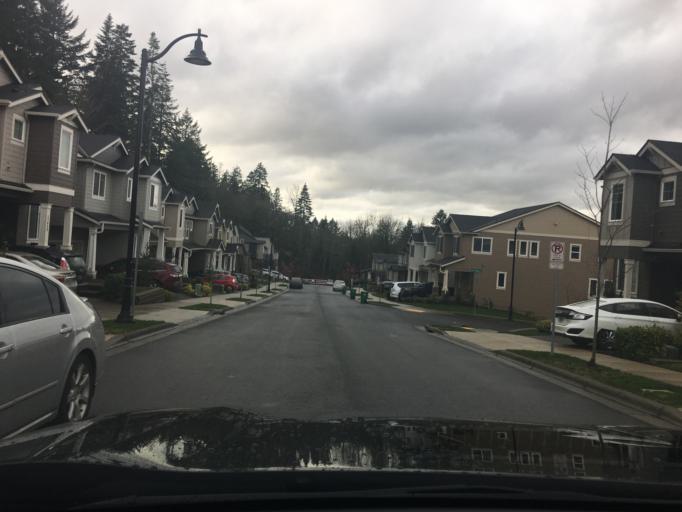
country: US
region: Oregon
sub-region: Washington County
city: Bethany
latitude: 45.5706
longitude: -122.8526
